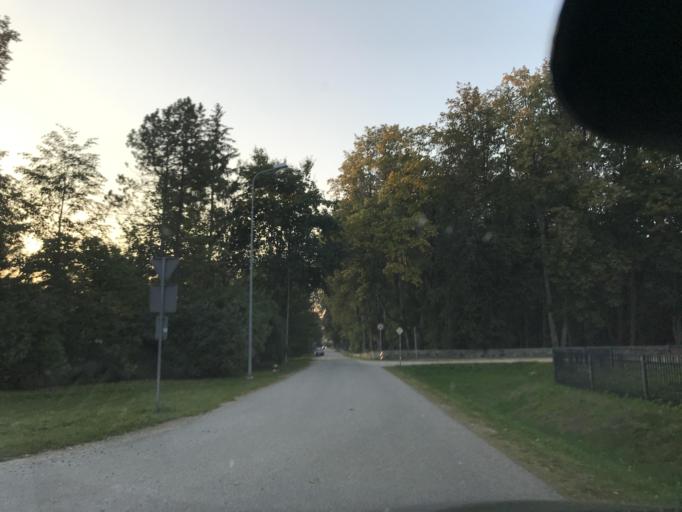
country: LV
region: Ikskile
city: Ikskile
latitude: 56.8299
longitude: 24.4961
